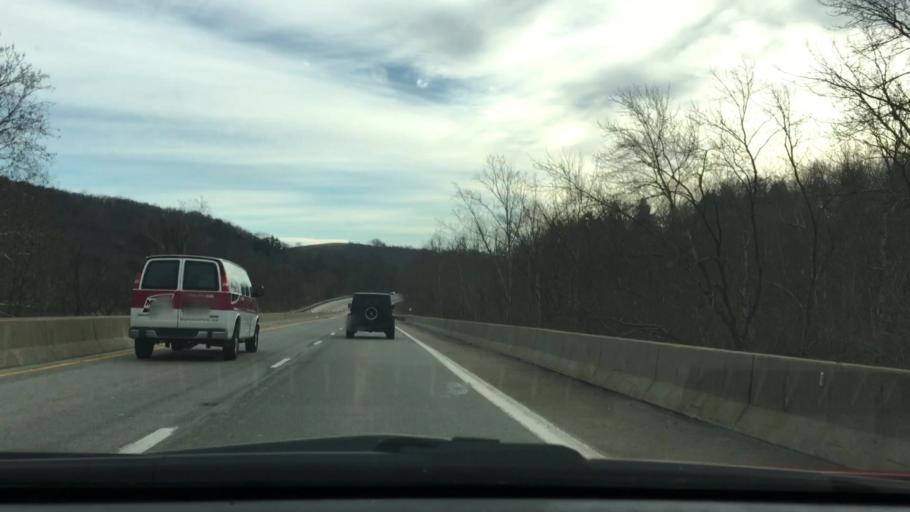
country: US
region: Pennsylvania
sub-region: Fayette County
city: Oliver
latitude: 39.9749
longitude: -79.7590
